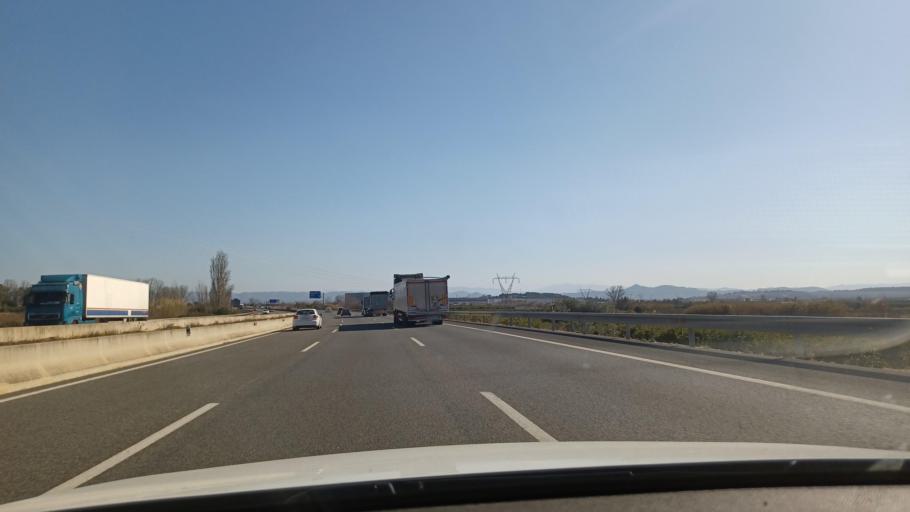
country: ES
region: Valencia
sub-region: Provincia de Valencia
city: Masalaves
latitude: 39.1437
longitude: -0.5296
